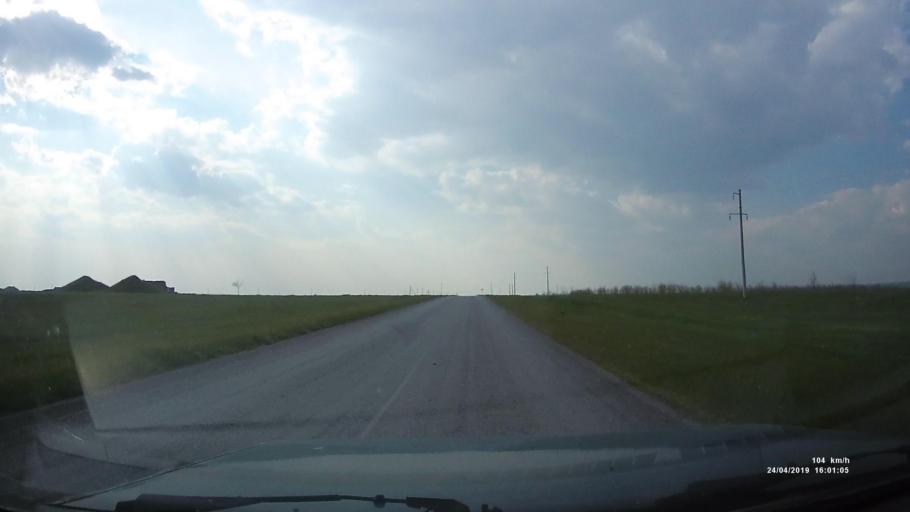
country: RU
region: Rostov
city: Sovetskoye
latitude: 46.6387
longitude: 42.4420
